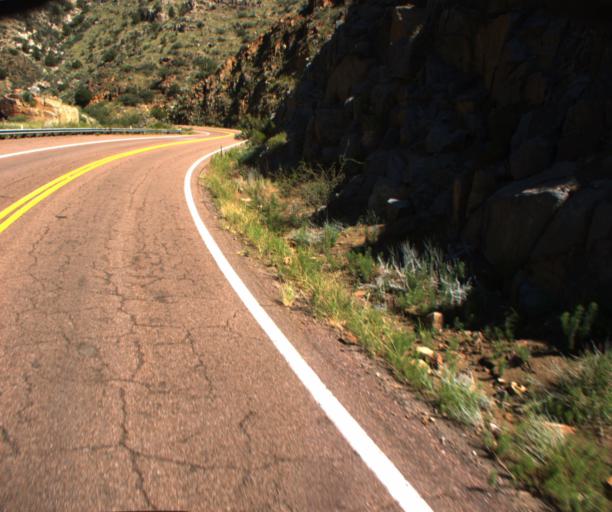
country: US
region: Arizona
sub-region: Navajo County
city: Cibecue
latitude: 33.8049
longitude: -110.4833
